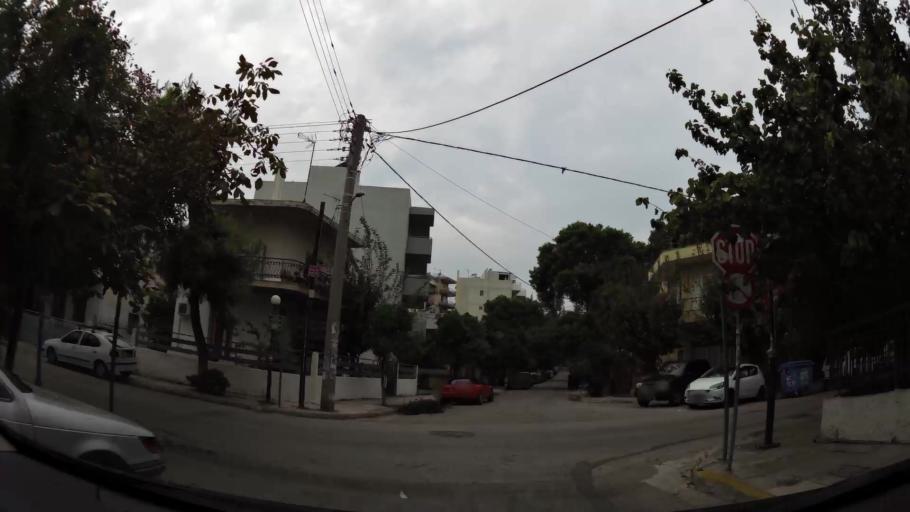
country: GR
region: Attica
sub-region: Nomarchia Athinas
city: Irakleio
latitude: 38.0404
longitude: 23.7704
